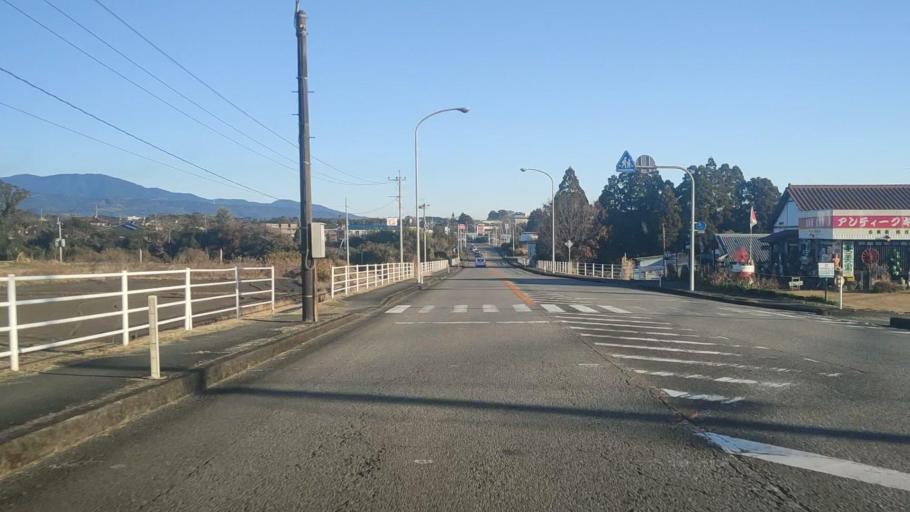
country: JP
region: Miyazaki
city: Takanabe
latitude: 32.1840
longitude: 131.5227
